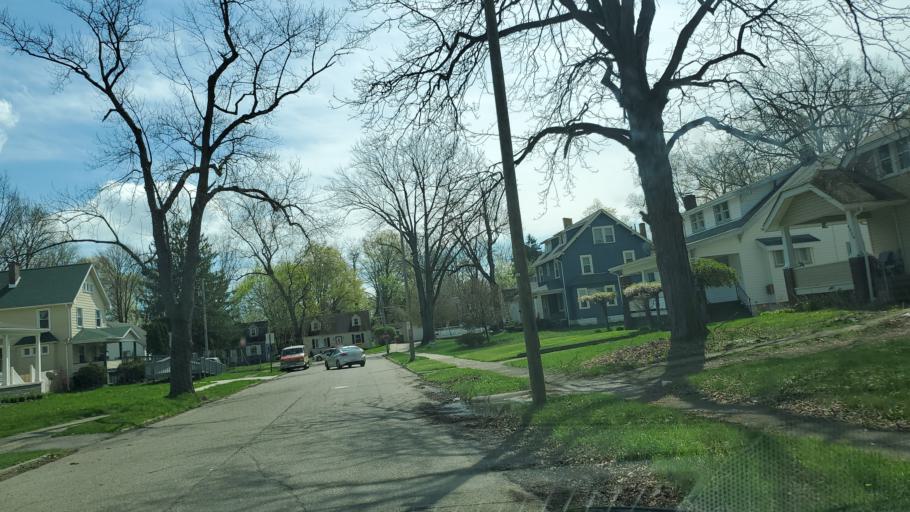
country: US
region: Ohio
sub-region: Mahoning County
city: Boardman
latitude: 41.0556
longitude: -80.6591
